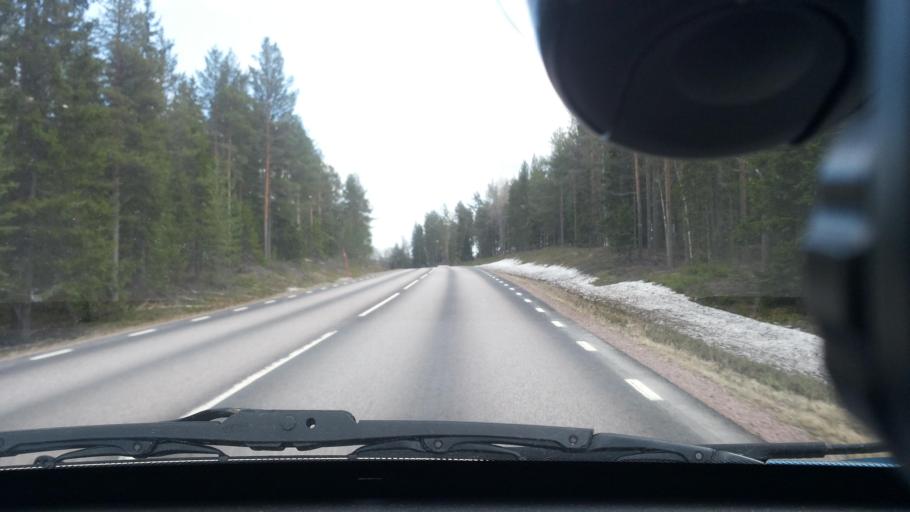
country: SE
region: Norrbotten
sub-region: Lulea Kommun
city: Sodra Sunderbyn
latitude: 65.6086
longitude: 21.9603
